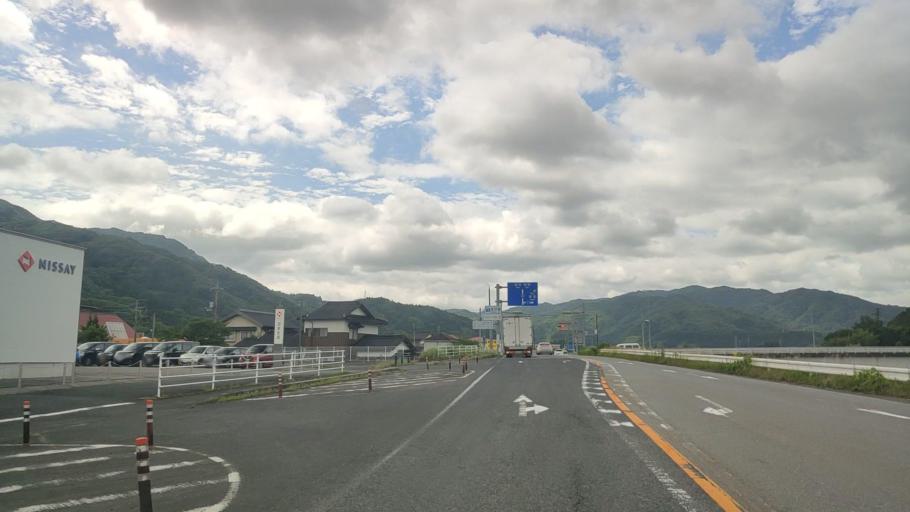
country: JP
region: Tottori
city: Yonago
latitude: 35.3432
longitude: 133.4350
